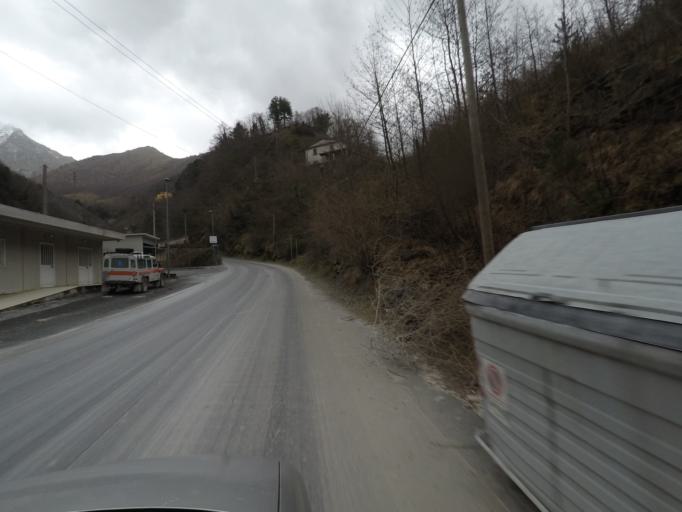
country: IT
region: Tuscany
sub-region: Provincia di Massa-Carrara
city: Montignoso
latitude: 44.0838
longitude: 10.1519
